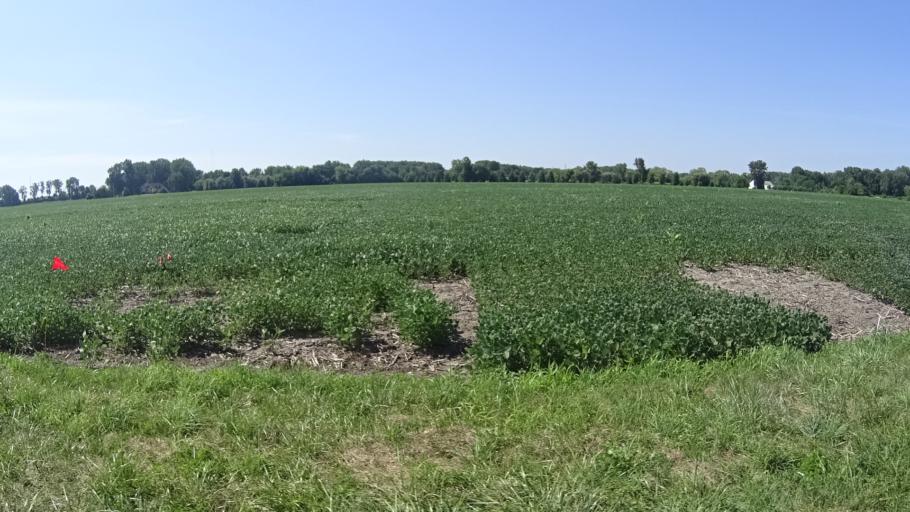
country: US
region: Ohio
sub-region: Erie County
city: Sandusky
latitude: 41.4258
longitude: -82.8063
